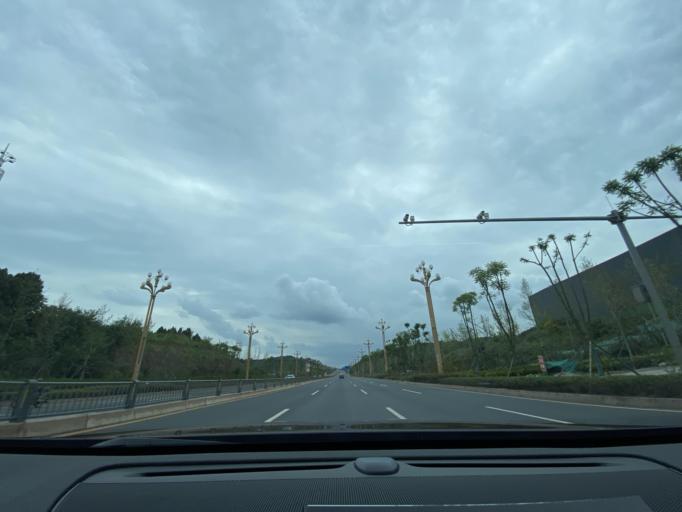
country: CN
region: Sichuan
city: Jiancheng
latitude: 30.4599
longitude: 104.4956
